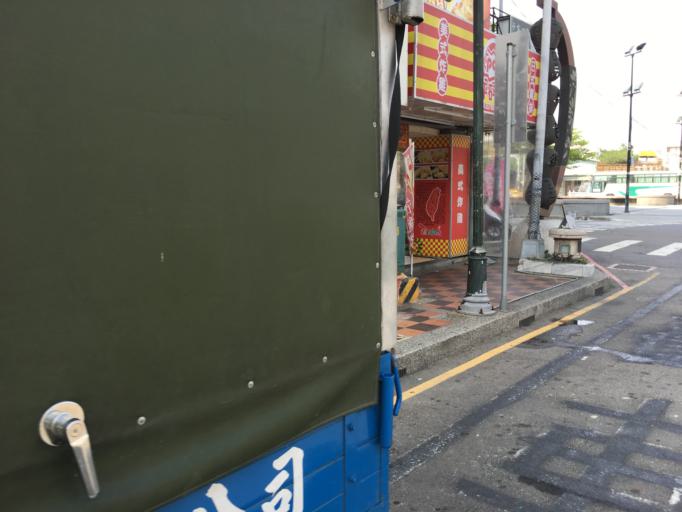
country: TW
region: Taiwan
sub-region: Changhua
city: Chang-hua
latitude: 24.0810
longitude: 120.5394
